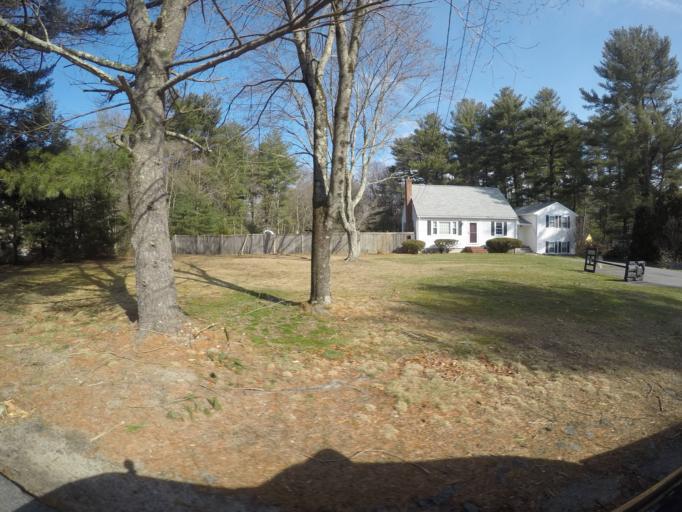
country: US
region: Massachusetts
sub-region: Bristol County
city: Easton
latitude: 42.0203
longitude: -71.1520
